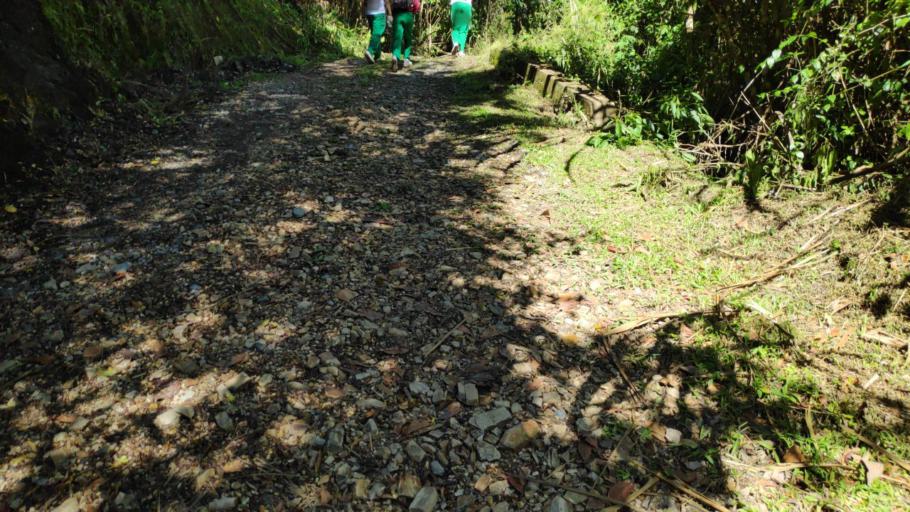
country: CO
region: Santander
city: Guepsa
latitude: 5.9885
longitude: -73.5424
